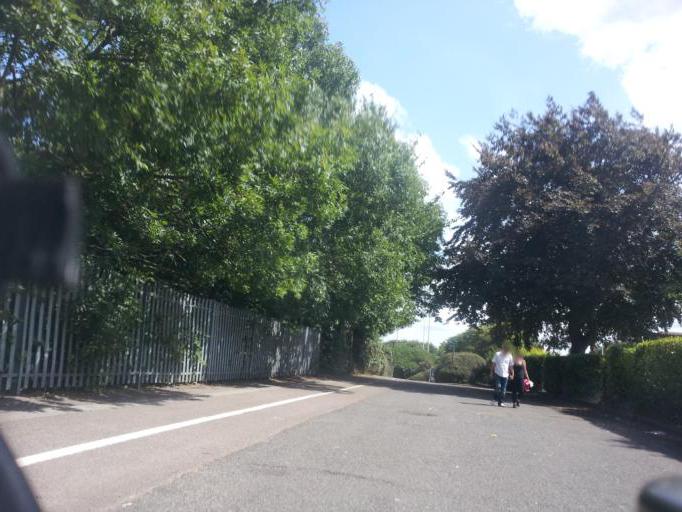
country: GB
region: England
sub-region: Kent
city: Gillingham
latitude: 51.3713
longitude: 0.5672
